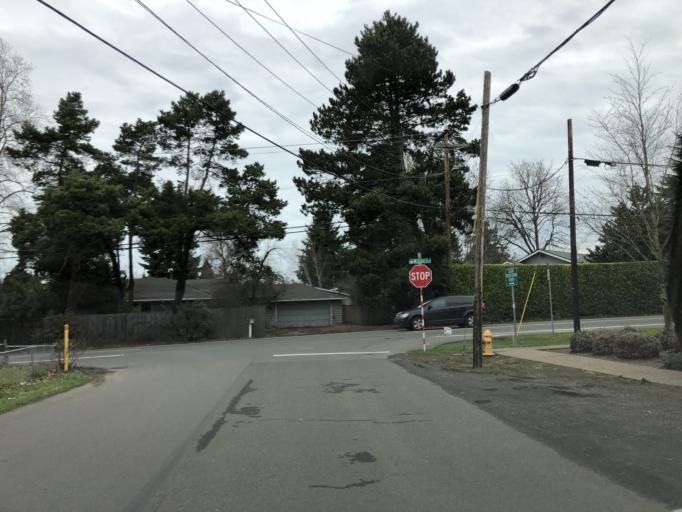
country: US
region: Oregon
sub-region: Washington County
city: Tigard
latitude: 45.4184
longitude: -122.7830
